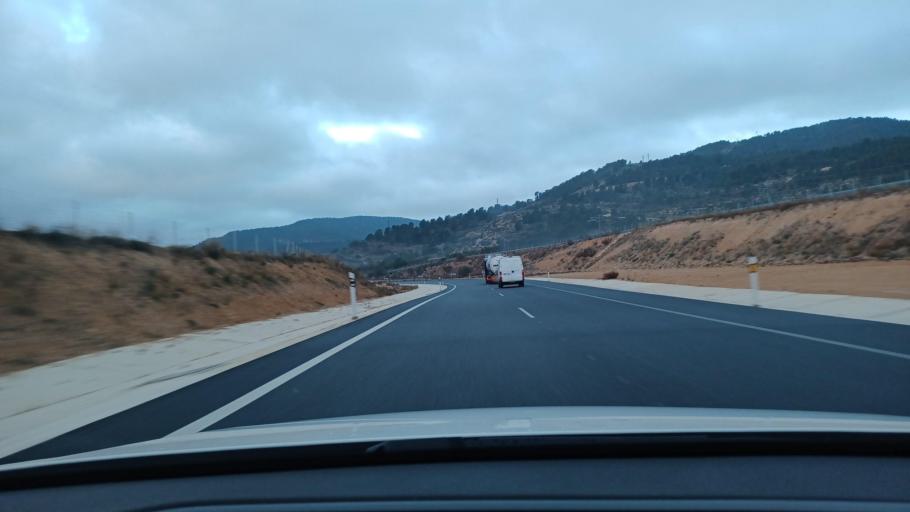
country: ES
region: Valencia
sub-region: Provincia de Valencia
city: La Font de la Figuera
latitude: 38.8304
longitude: -0.8860
